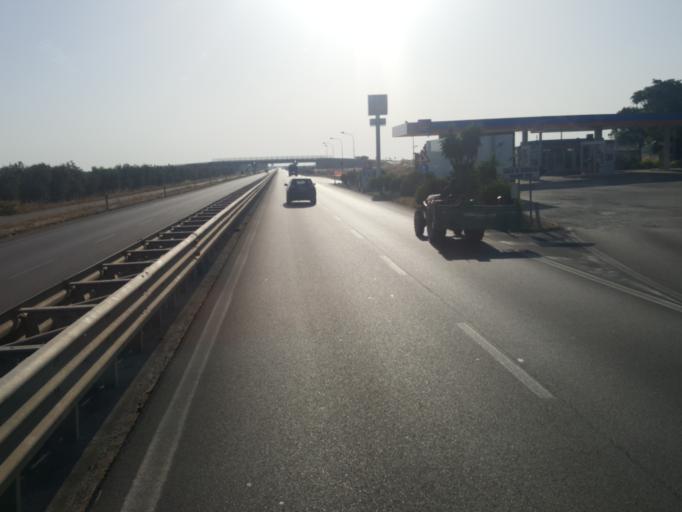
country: IT
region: Apulia
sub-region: Provincia di Barletta - Andria - Trani
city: Trinitapoli
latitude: 41.3166
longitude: 16.1182
